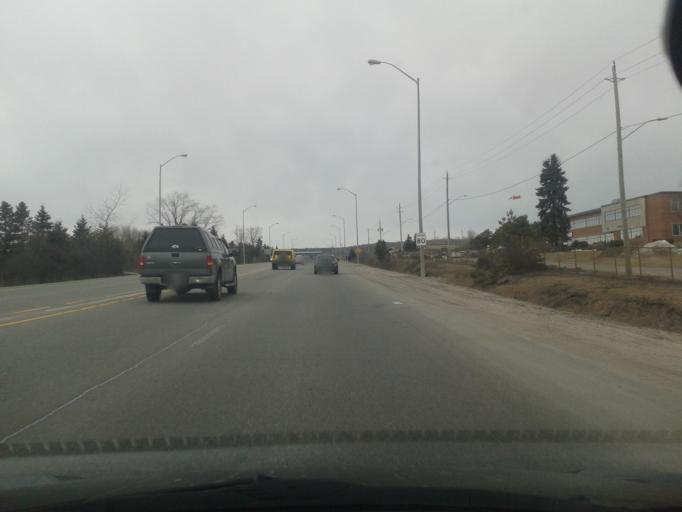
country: CA
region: Ontario
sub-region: Nipissing District
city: North Bay
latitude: 46.3213
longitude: -79.4455
